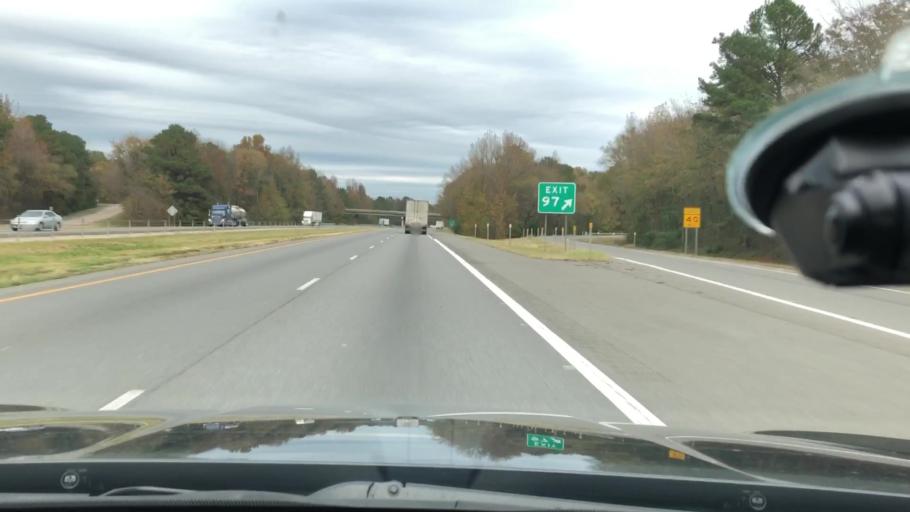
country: US
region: Arkansas
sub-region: Hot Spring County
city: Malvern
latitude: 34.3832
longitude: -92.8480
